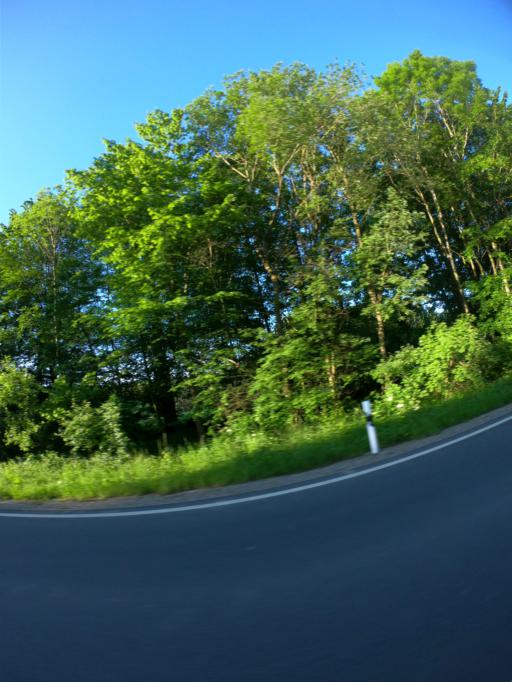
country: DE
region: Bavaria
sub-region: Upper Bavaria
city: Fraunberg
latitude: 48.3381
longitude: 12.0229
